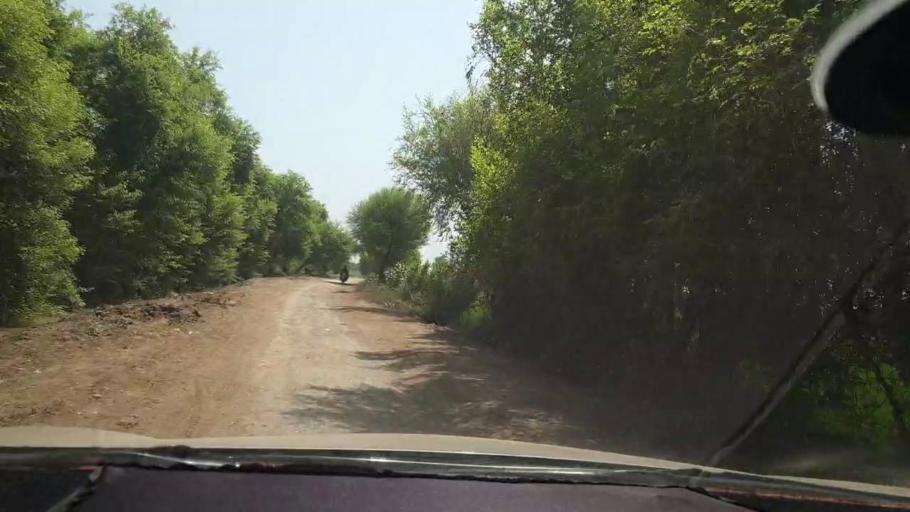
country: PK
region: Sindh
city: Kambar
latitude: 27.6708
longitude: 67.9426
